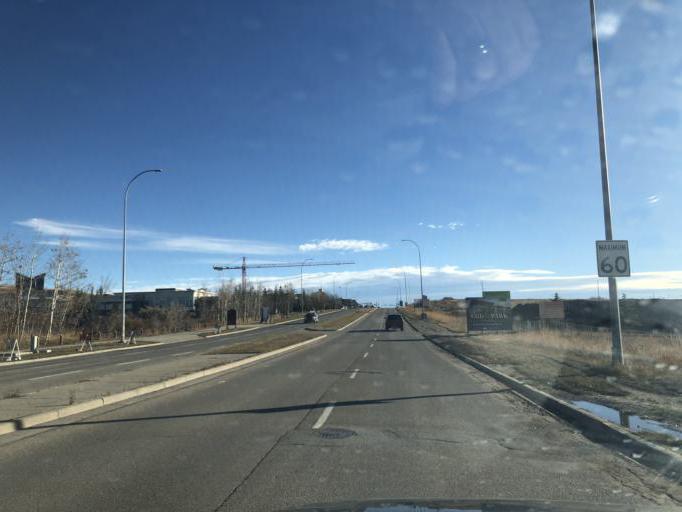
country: CA
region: Alberta
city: Calgary
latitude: 51.0379
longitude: -114.2101
